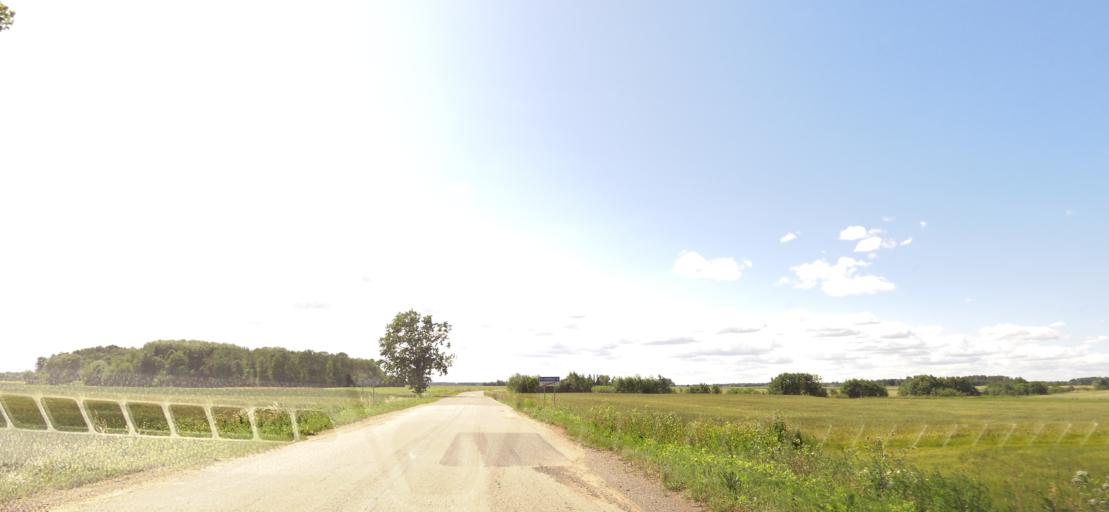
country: LV
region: Bauskas Rajons
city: Bauska
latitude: 56.2394
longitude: 24.2241
